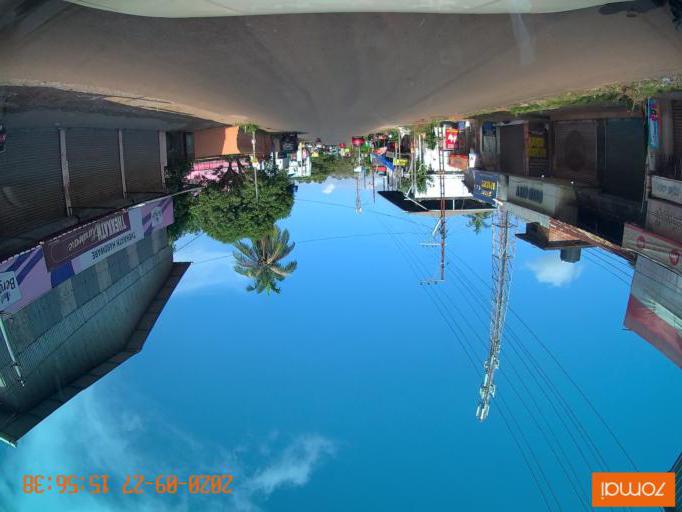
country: IN
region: Kerala
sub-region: Thrissur District
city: Trichur
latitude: 10.5179
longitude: 76.1802
